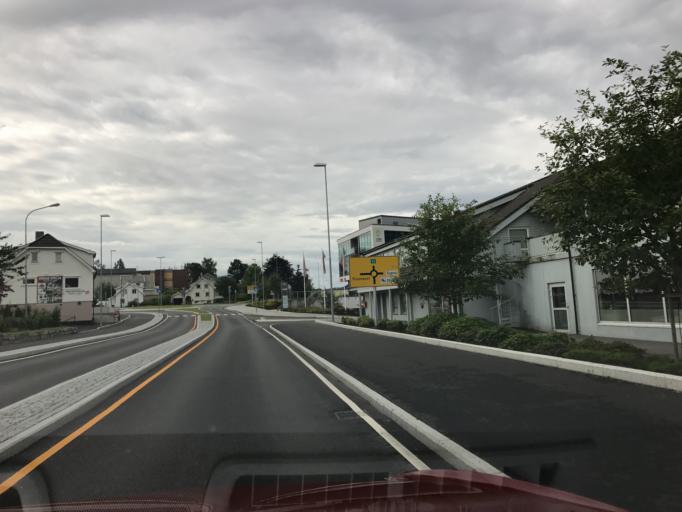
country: NO
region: Rogaland
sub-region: Strand
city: Jorpeland
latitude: 59.0228
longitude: 6.0442
